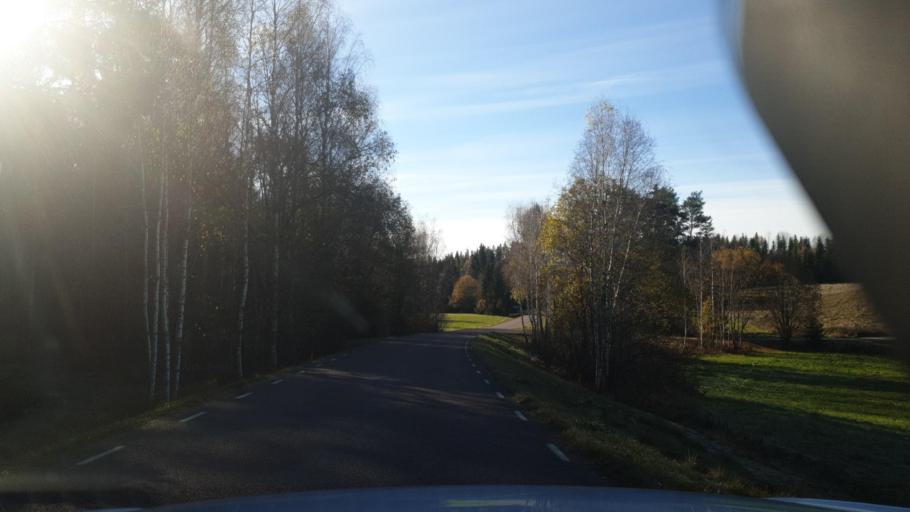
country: SE
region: Vaermland
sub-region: Karlstads Kommun
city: Edsvalla
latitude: 59.4965
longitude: 13.1057
